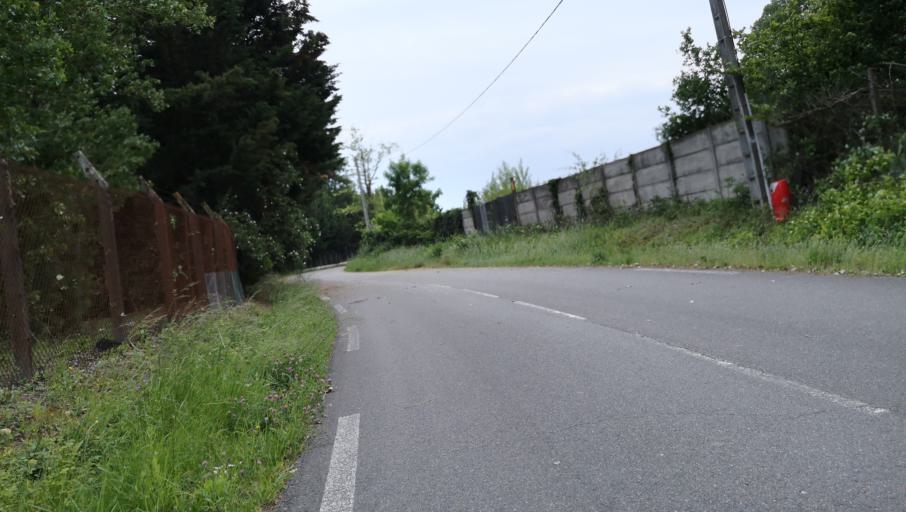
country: FR
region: Centre
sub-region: Departement du Loiret
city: Fleury-les-Aubrais
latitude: 47.9486
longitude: 1.9111
